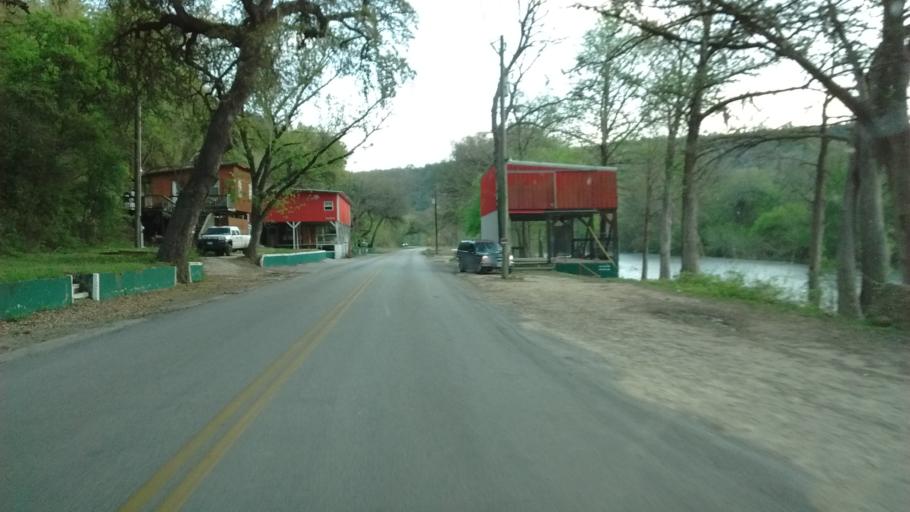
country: US
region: Texas
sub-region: Comal County
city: New Braunfels
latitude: 29.7708
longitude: -98.1584
